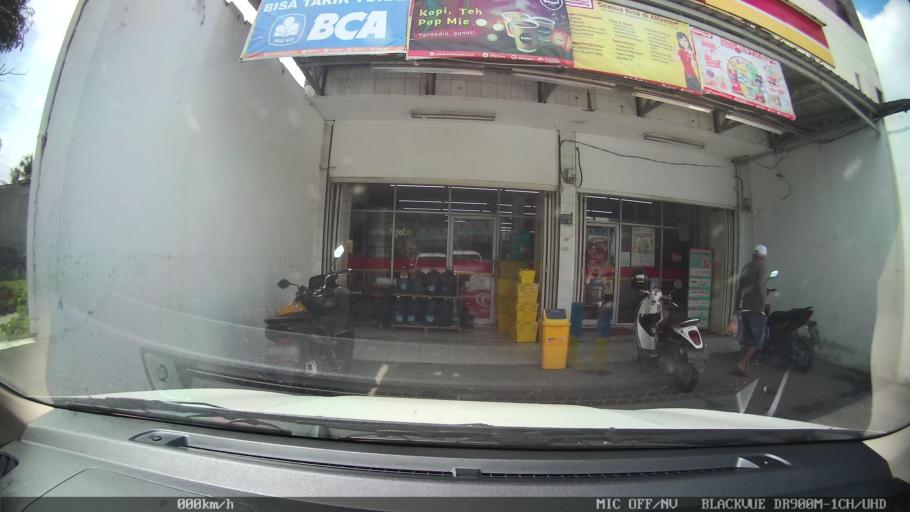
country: ID
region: North Sumatra
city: Percut
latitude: 3.6070
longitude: 98.7836
